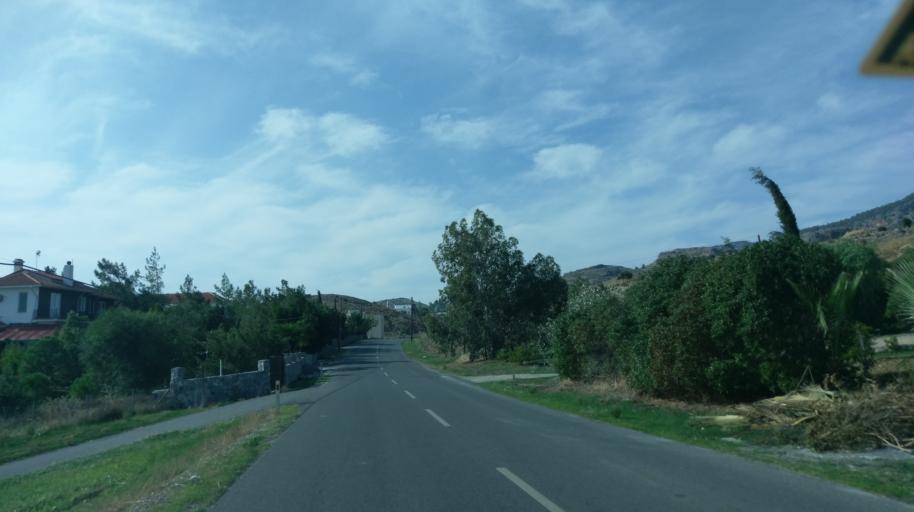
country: CY
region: Keryneia
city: Kyrenia
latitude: 35.2846
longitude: 33.2490
